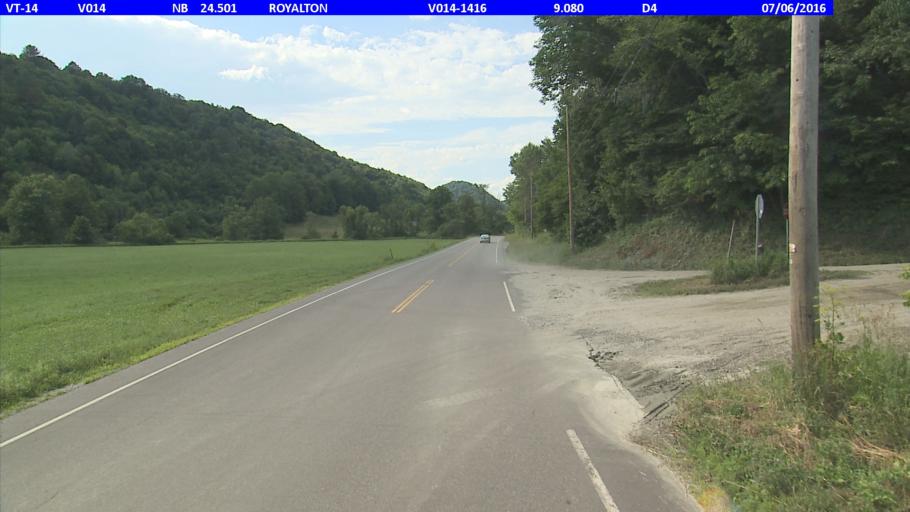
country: US
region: Vermont
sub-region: Orange County
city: Randolph
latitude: 43.8627
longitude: -72.5820
